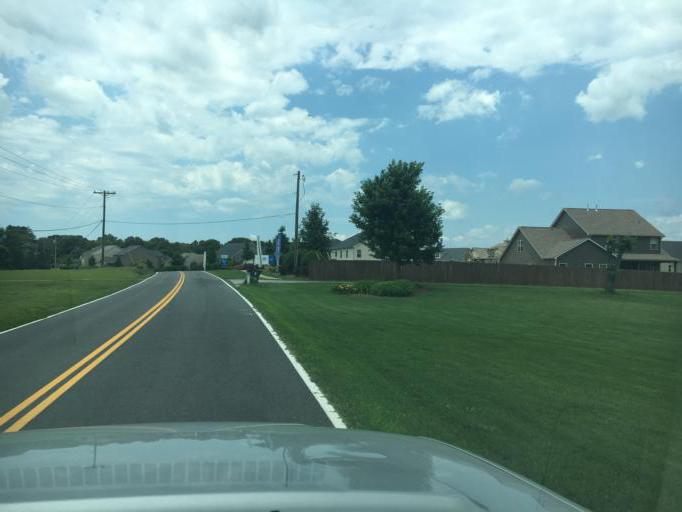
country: US
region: South Carolina
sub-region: Spartanburg County
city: Duncan
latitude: 34.8746
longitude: -82.1705
